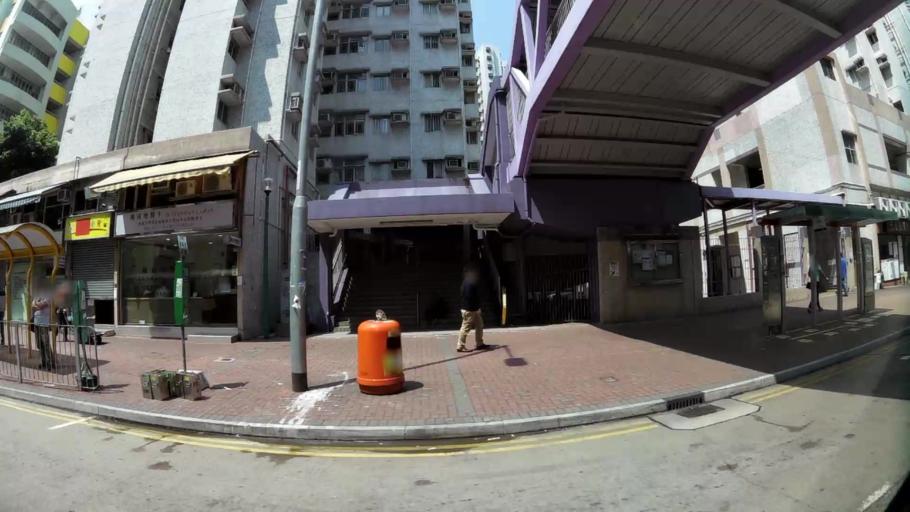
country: HK
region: Sham Shui Po
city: Sham Shui Po
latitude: 22.3145
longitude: 114.1642
